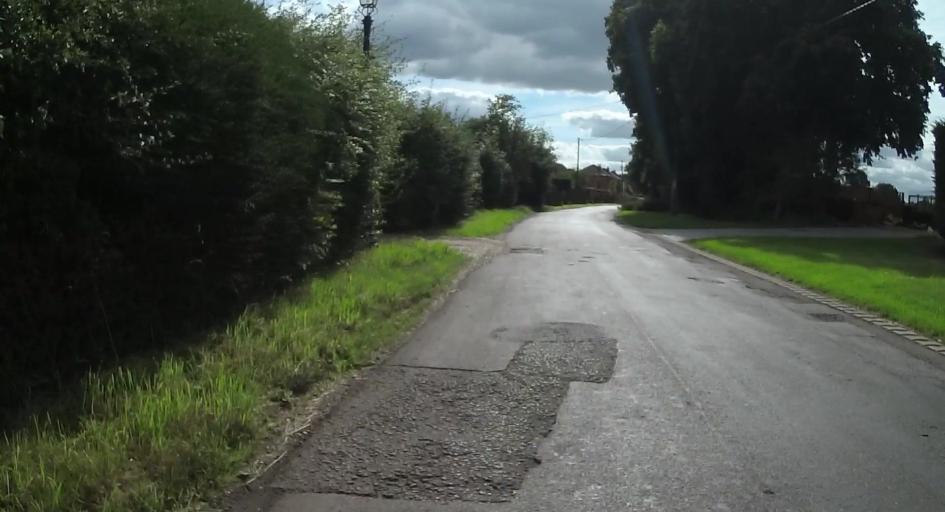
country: GB
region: England
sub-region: Surrey
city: Chobham
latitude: 51.3439
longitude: -0.6176
